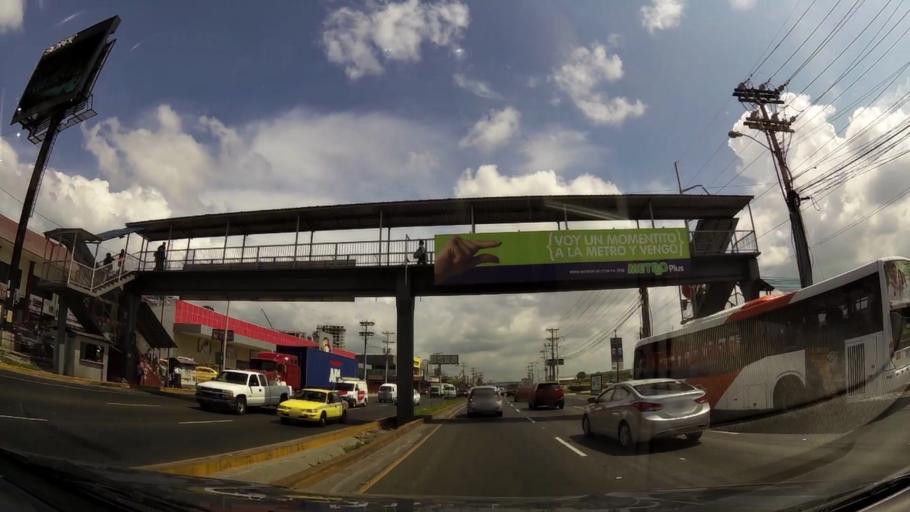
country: PA
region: Panama
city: San Miguelito
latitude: 9.0435
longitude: -79.4721
